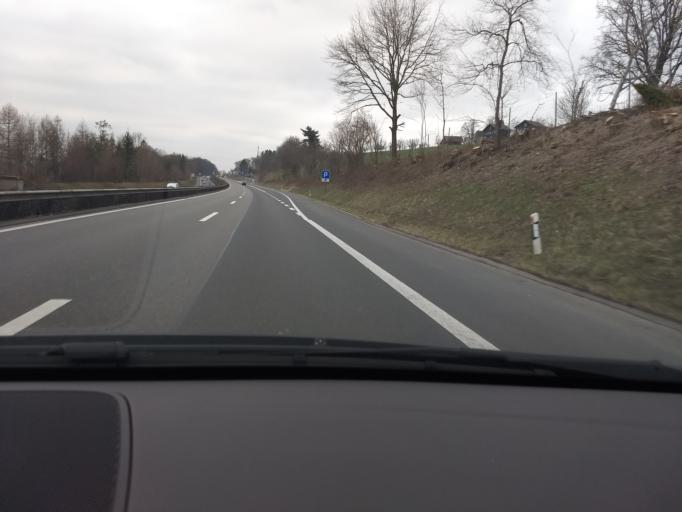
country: CH
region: Lucerne
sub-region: Sursee District
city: Sempach
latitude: 47.1420
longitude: 8.1897
